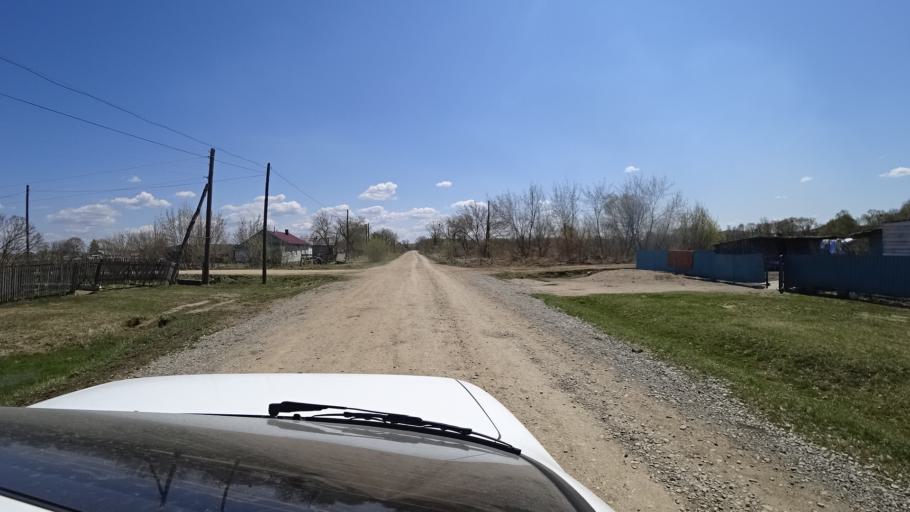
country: RU
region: Primorskiy
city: Dal'nerechensk
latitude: 45.8014
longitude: 133.7654
